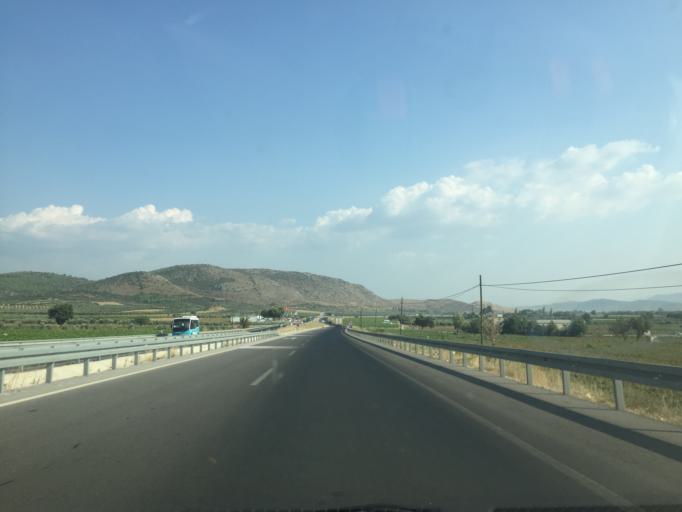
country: TR
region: Manisa
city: Golmarmara
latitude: 38.7937
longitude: 27.8986
